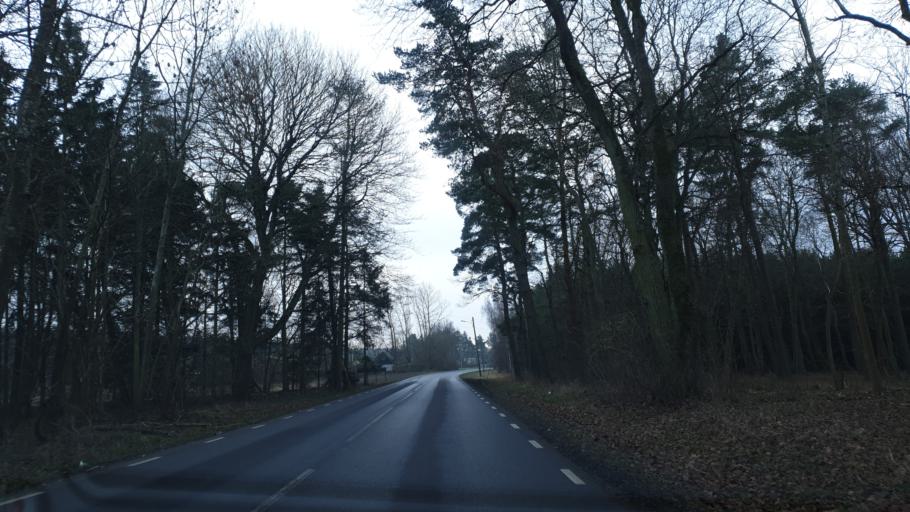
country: SE
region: Skane
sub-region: Kristianstads Kommun
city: Fjalkinge
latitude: 56.0181
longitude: 14.3729
